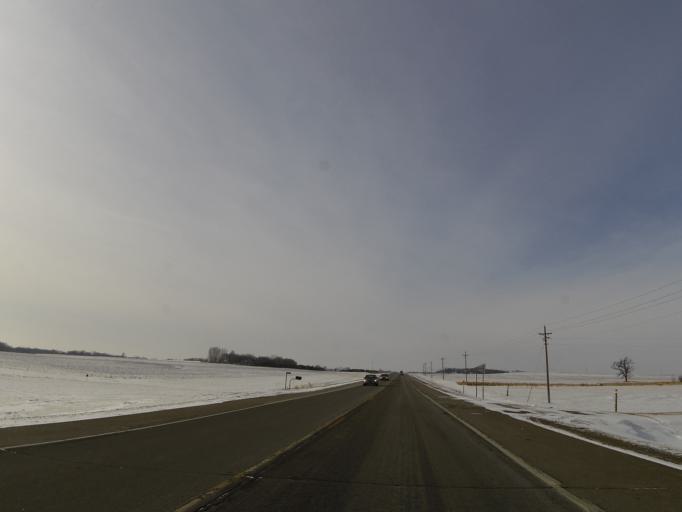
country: US
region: Minnesota
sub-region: McLeod County
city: Lester Prairie
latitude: 44.9067
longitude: -93.9812
